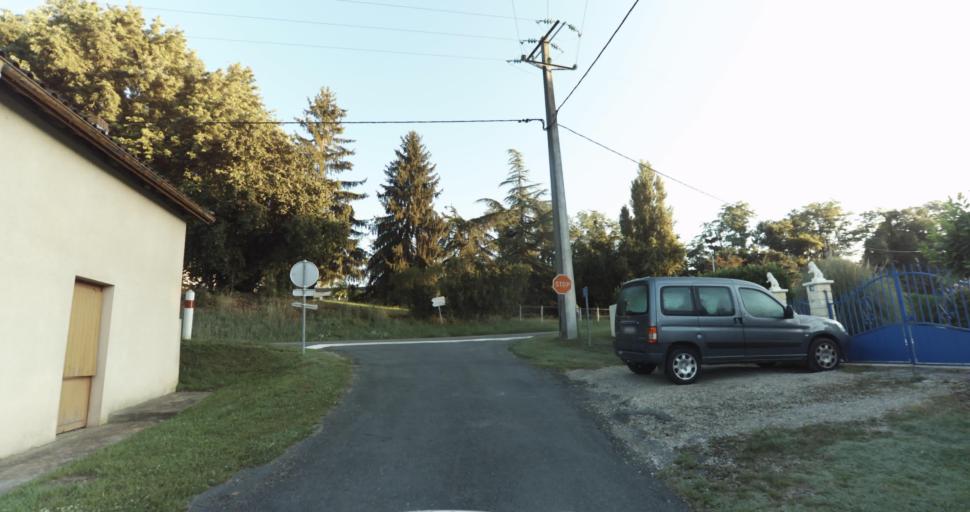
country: FR
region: Aquitaine
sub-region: Departement de la Gironde
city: Bazas
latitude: 44.4301
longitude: -0.2243
